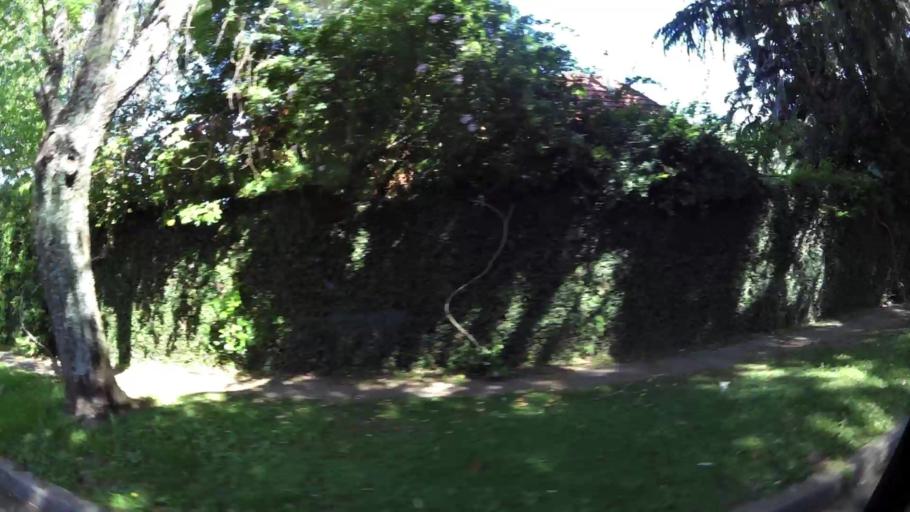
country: AR
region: Buenos Aires
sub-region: Partido de San Isidro
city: San Isidro
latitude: -34.4565
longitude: -58.5248
